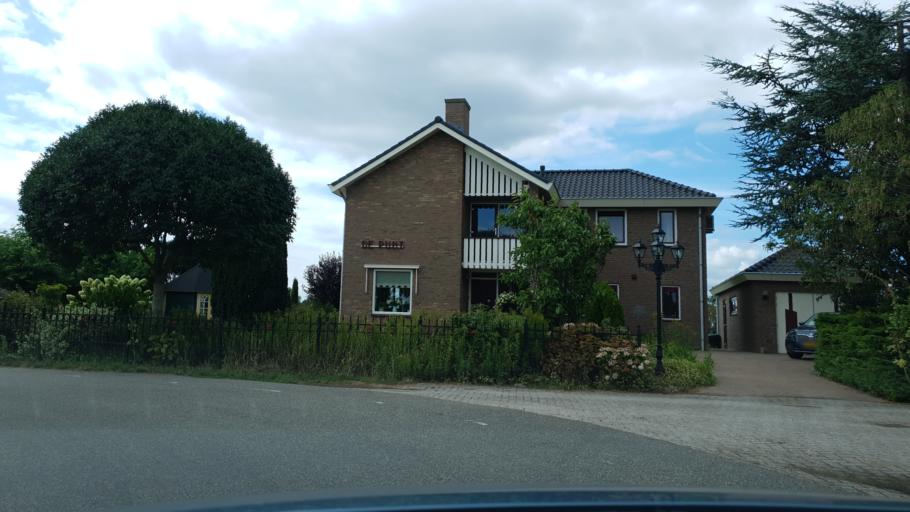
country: NL
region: North Brabant
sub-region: Gemeente Grave
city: Grave
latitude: 51.7618
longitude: 5.7923
